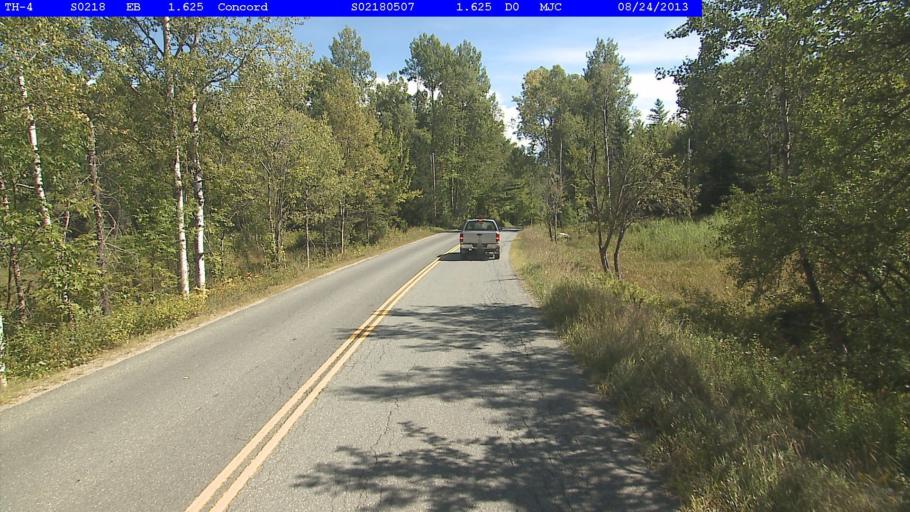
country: US
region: New Hampshire
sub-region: Grafton County
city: Littleton
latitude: 44.4435
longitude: -71.7633
